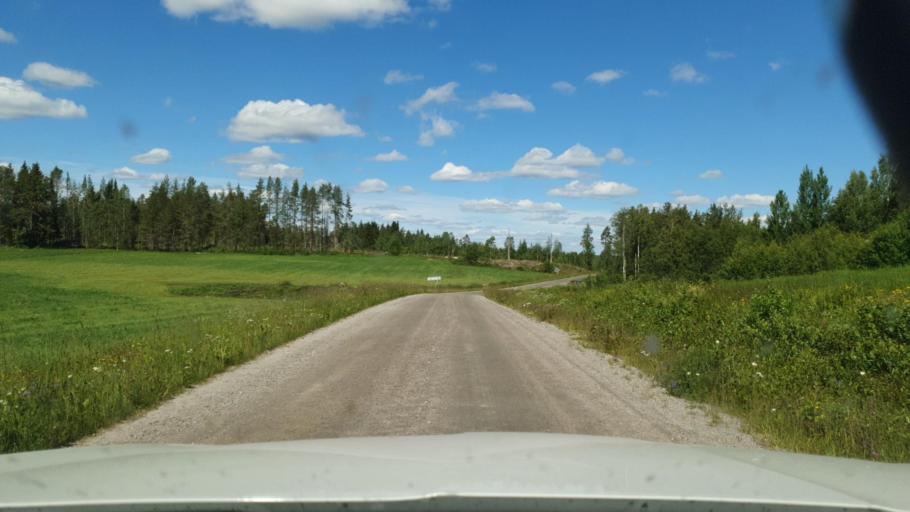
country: SE
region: Vaesterbotten
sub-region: Skelleftea Kommun
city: Byske
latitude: 65.1230
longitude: 21.2054
